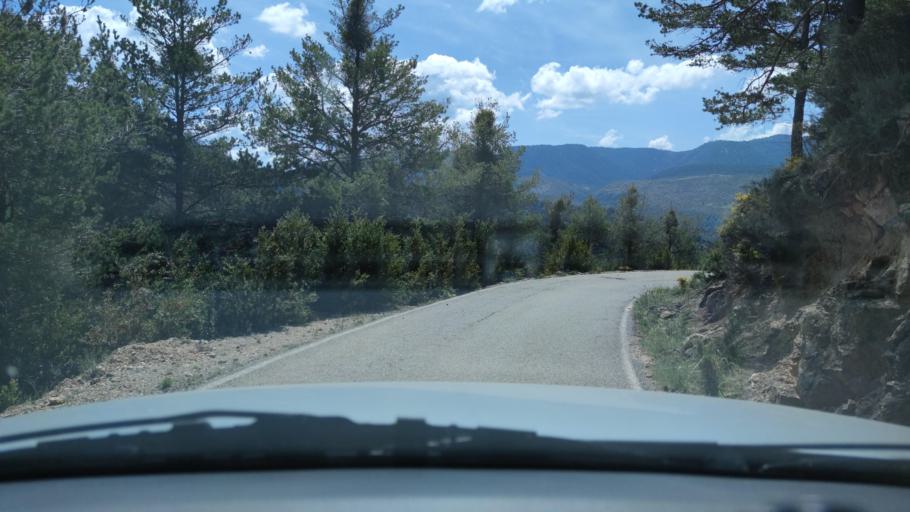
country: ES
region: Catalonia
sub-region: Provincia de Lleida
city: Sort
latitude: 42.3083
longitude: 1.1268
